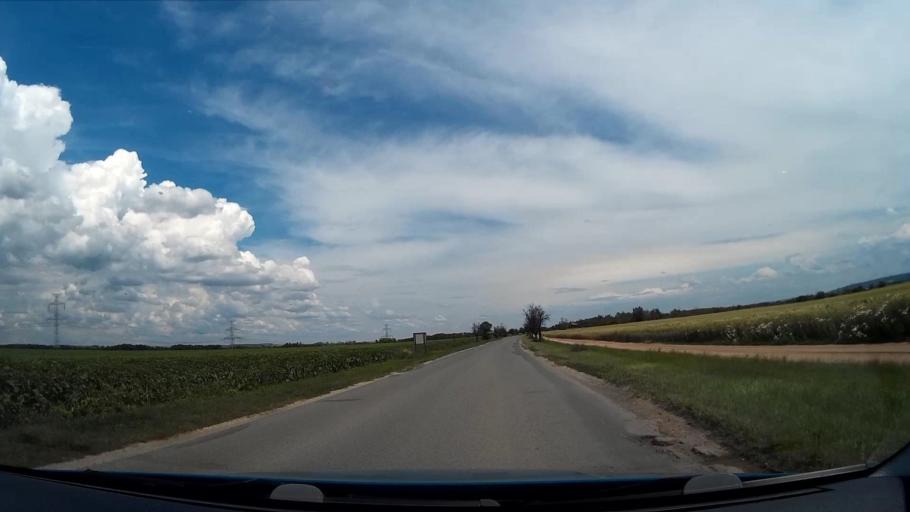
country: CZ
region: South Moravian
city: Dolni Kounice
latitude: 49.0554
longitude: 16.5080
